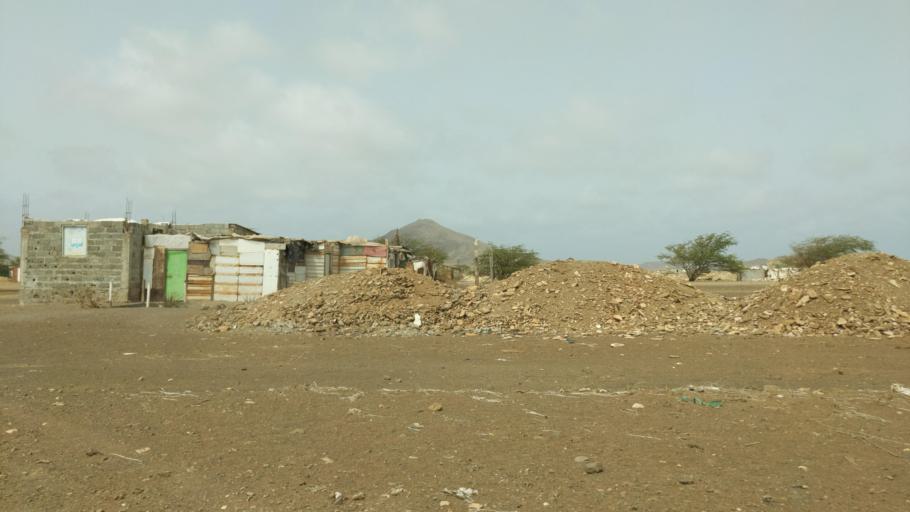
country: CV
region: Sal
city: Espargos
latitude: 16.7719
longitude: -22.9468
